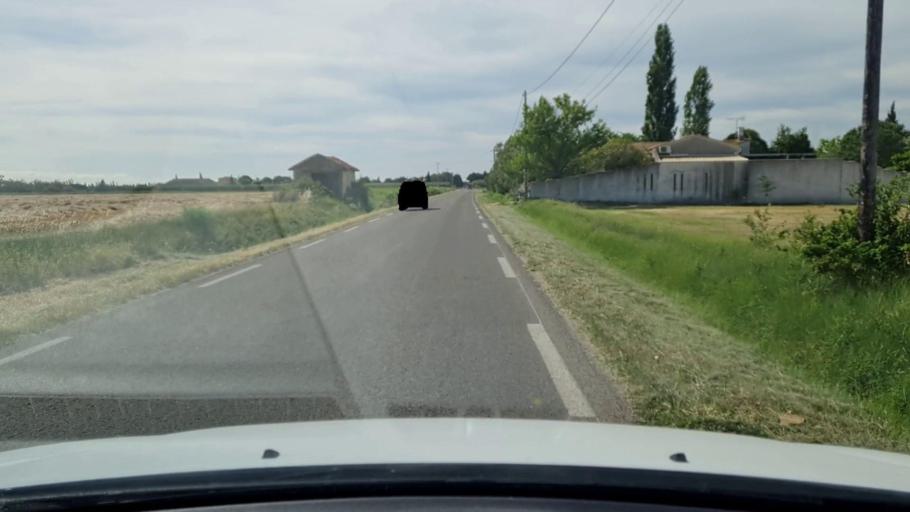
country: FR
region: Languedoc-Roussillon
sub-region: Departement de l'Herault
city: Marsillargues
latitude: 43.6221
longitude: 4.2016
